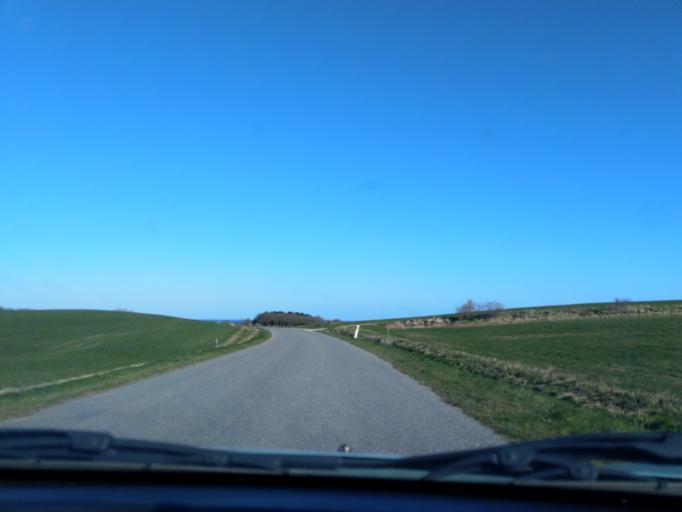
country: DK
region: Zealand
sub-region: Kalundborg Kommune
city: Kalundborg
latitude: 55.7409
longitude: 10.9552
